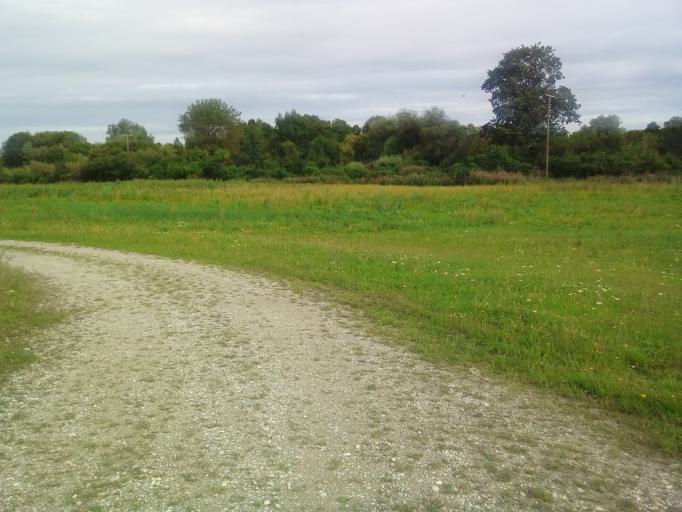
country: DE
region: Bavaria
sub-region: Upper Bavaria
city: Ismaning
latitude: 48.1989
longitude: 11.6789
